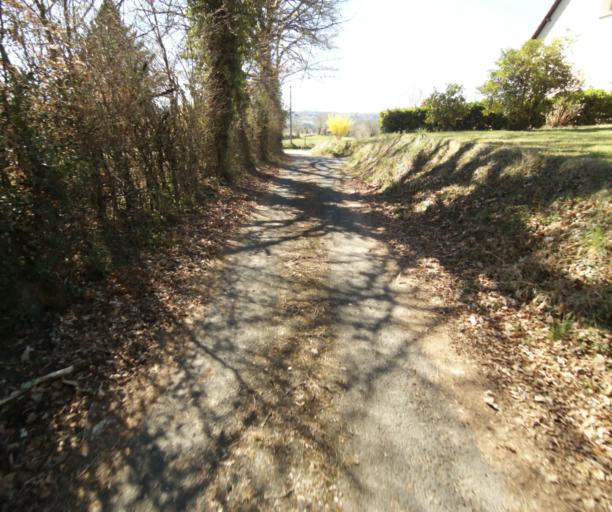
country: FR
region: Limousin
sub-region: Departement de la Correze
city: Chamboulive
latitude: 45.4341
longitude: 1.7155
